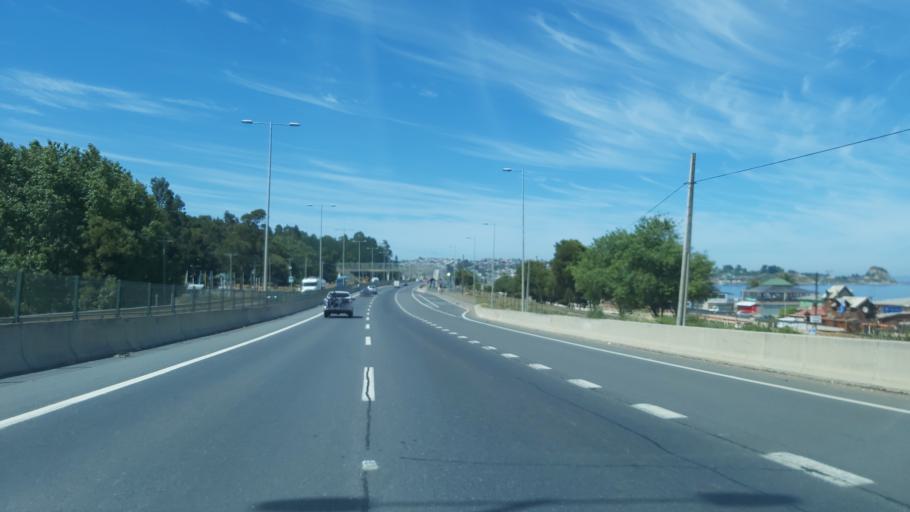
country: CL
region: Biobio
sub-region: Provincia de Concepcion
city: Coronel
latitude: -37.0610
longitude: -73.1407
